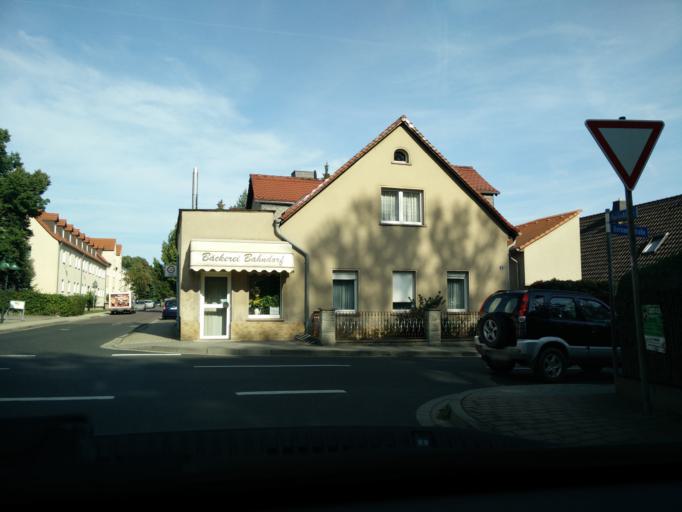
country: DE
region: Saxony
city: Kitzscher
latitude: 51.1613
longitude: 12.5541
